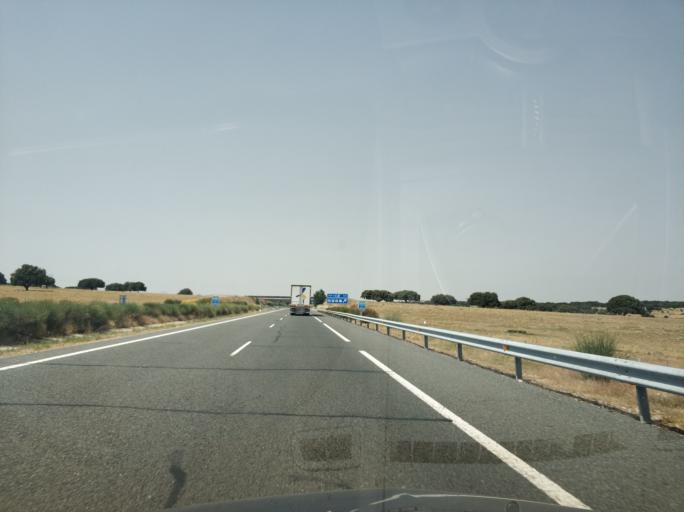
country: ES
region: Castille and Leon
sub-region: Provincia de Salamanca
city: Buenavista
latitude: 40.7872
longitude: -5.6335
